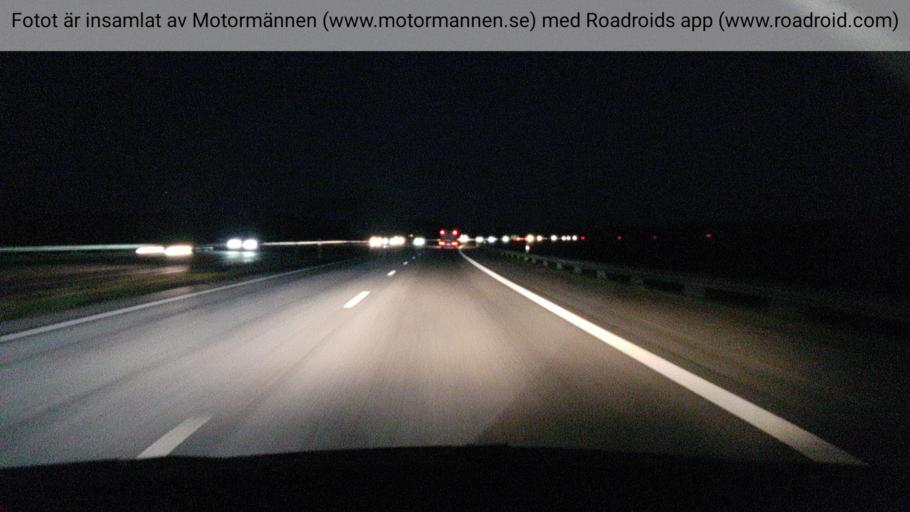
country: SE
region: Uppsala
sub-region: Uppsala Kommun
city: Saevja
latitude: 59.8217
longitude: 17.7466
